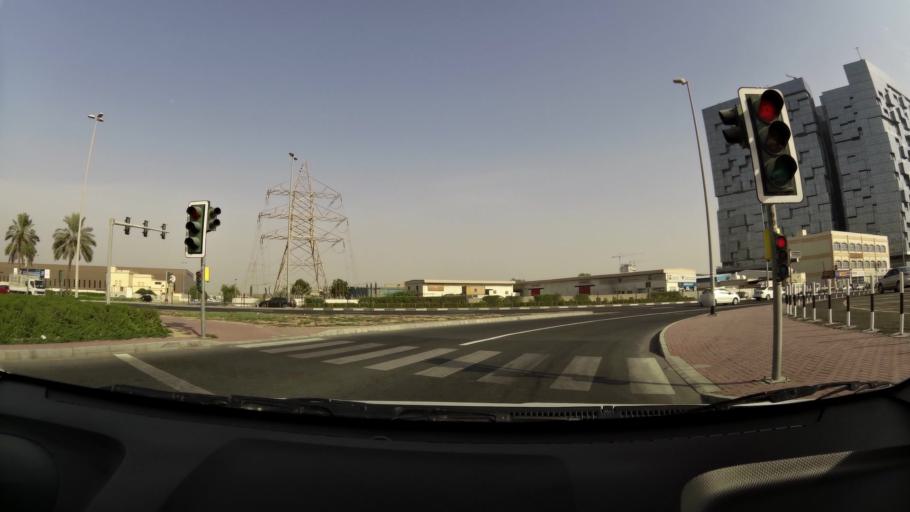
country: AE
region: Ash Shariqah
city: Sharjah
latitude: 25.2320
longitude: 55.3555
